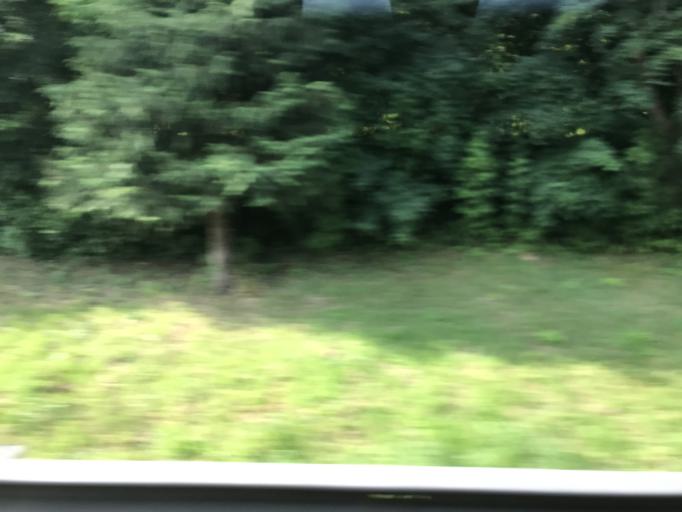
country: ES
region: Basque Country
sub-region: Provincia de Guipuzcoa
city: Legorreta
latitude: 43.0831
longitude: -2.1435
